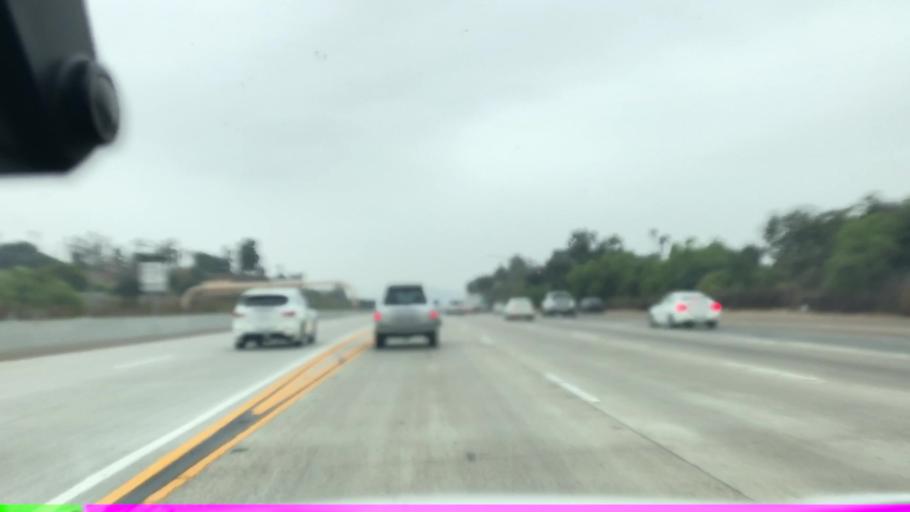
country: US
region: California
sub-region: San Diego County
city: Escondido
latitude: 33.0904
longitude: -117.0807
